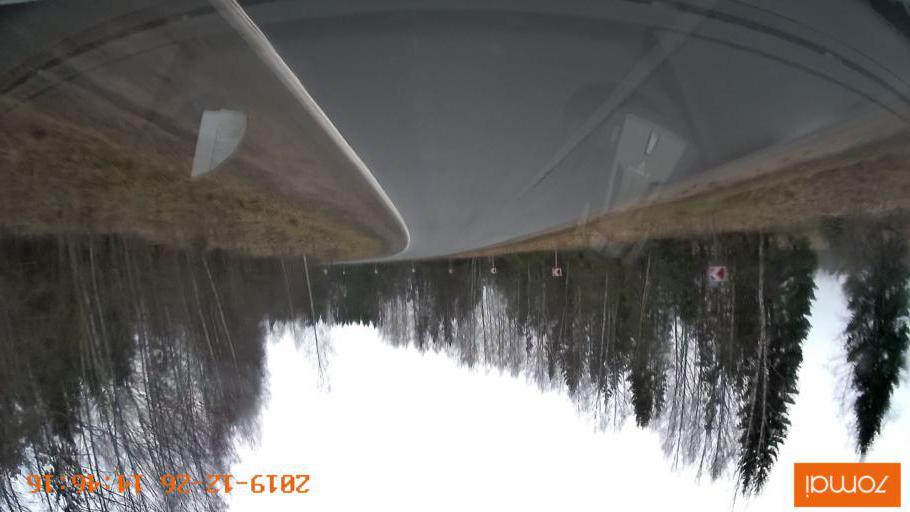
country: RU
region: Jaroslavl
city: Poshekhon'ye
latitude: 58.3350
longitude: 39.0202
